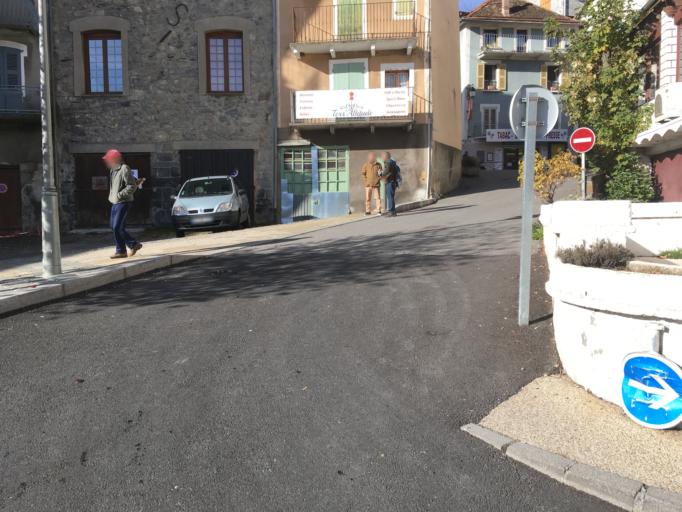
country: FR
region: Provence-Alpes-Cote d'Azur
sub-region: Departement des Alpes-de-Haute-Provence
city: Seyne-les-Alpes
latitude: 44.3513
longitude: 6.3564
